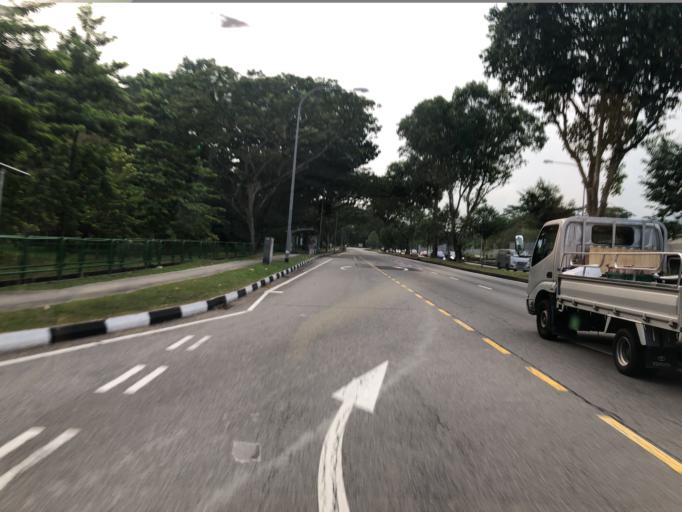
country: MY
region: Johor
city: Kampung Pasir Gudang Baru
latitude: 1.3946
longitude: 103.8331
